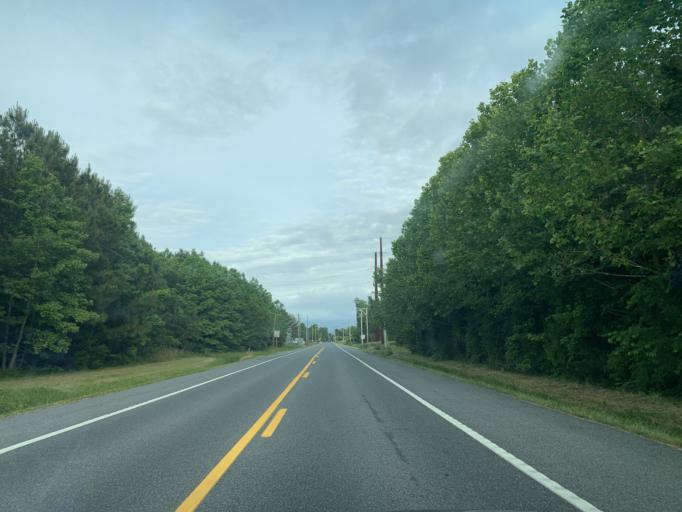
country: US
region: Virginia
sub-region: Accomack County
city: Captains Cove
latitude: 38.0576
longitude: -75.4196
